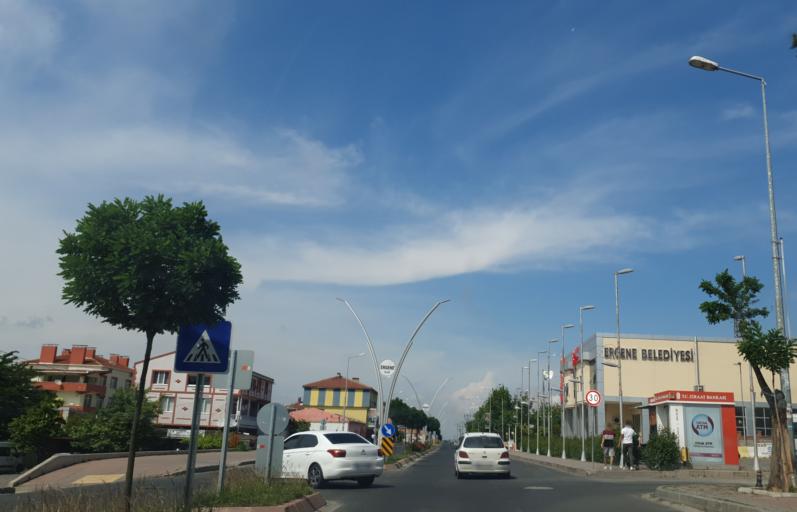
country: TR
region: Tekirdag
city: Marmaracik
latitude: 41.2374
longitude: 27.7096
